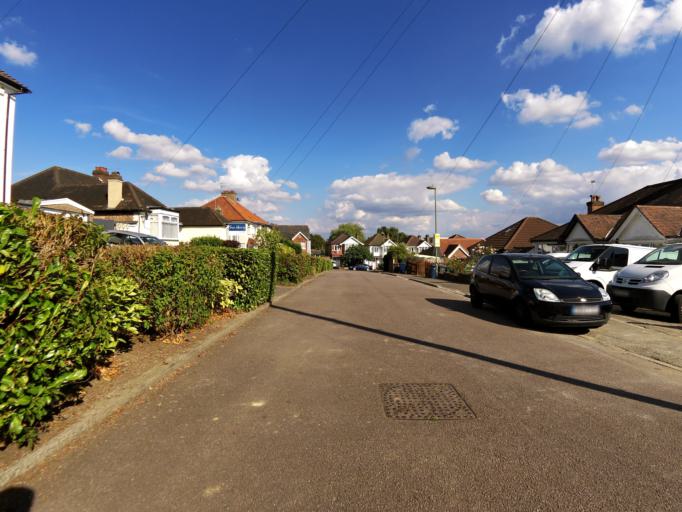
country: GB
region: England
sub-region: Greater London
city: Hadley Wood
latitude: 51.6442
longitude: -0.1741
